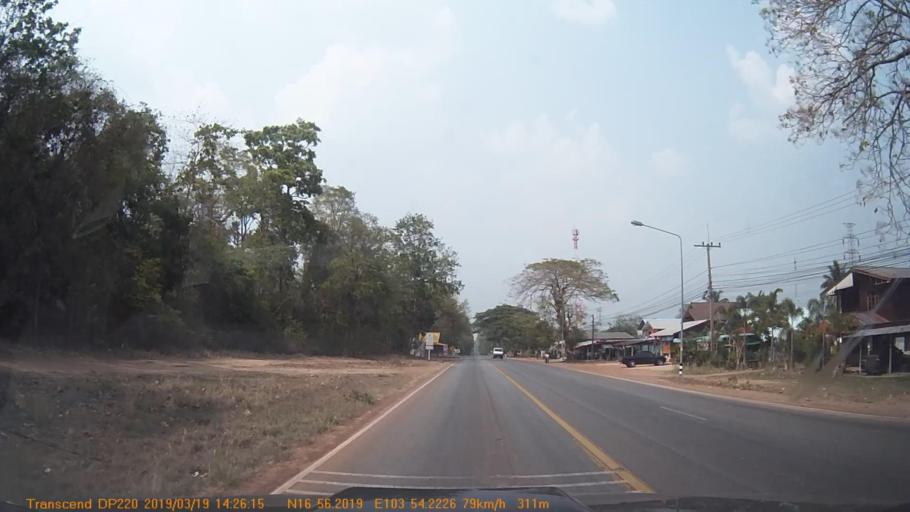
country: TH
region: Sakon Nakhon
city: Phu Phan
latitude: 16.9372
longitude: 103.9037
